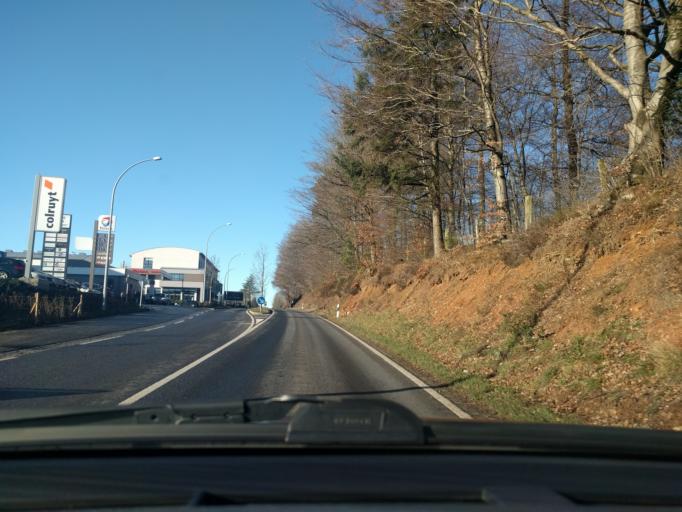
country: LU
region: Diekirch
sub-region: Canton de Clervaux
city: Weiswampach
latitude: 50.1565
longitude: 6.0508
